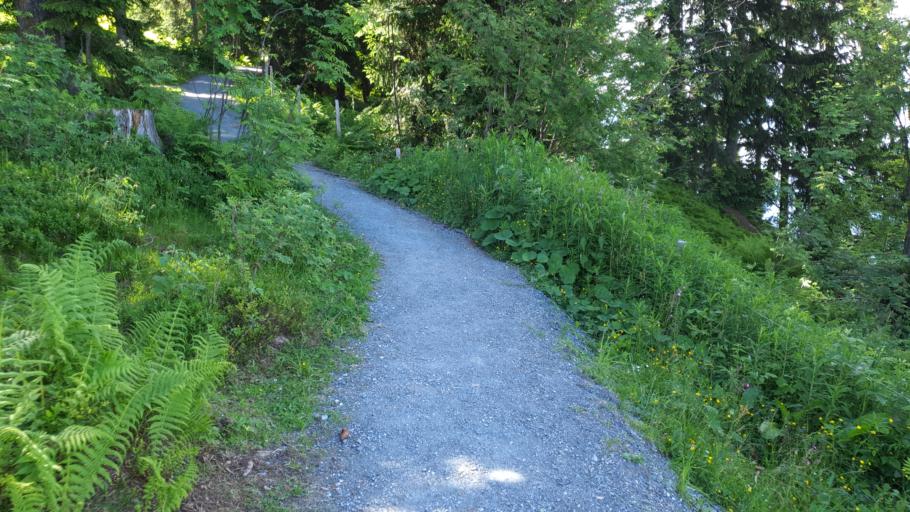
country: AT
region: Tyrol
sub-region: Politischer Bezirk Kitzbuhel
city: Brixen im Thale
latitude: 47.4895
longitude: 12.2519
